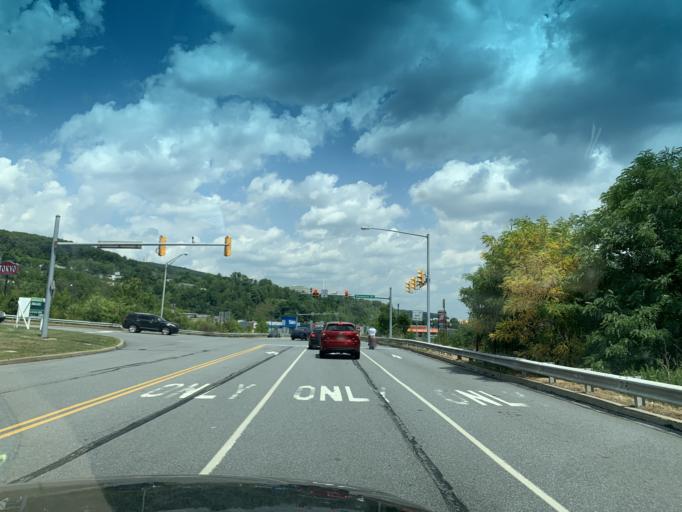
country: US
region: Pennsylvania
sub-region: Lackawanna County
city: Chinchilla
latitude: 41.4605
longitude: -75.6502
